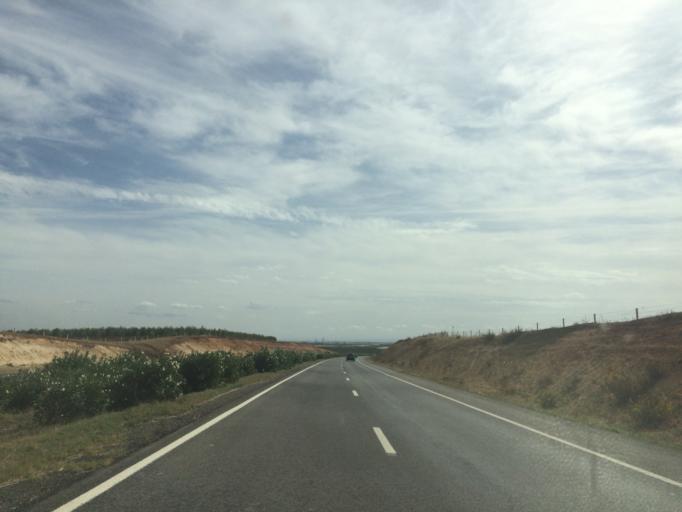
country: MA
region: Meknes-Tafilalet
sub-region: Meknes
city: Meknes
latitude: 33.8915
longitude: -5.6682
